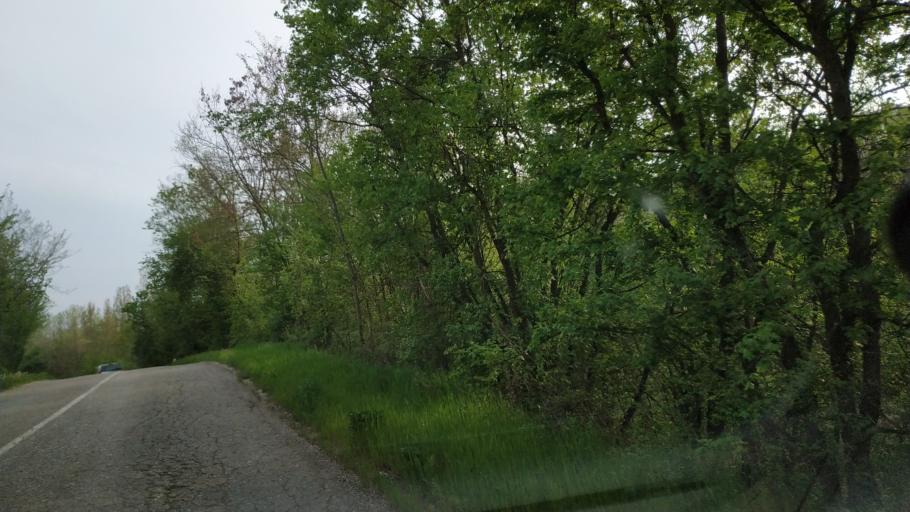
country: RS
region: Central Serbia
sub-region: Nisavski Okrug
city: Aleksinac
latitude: 43.4762
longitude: 21.8106
